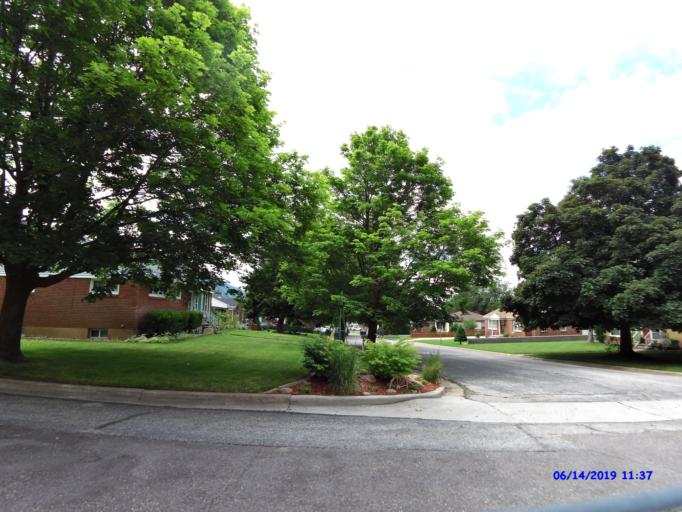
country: US
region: Utah
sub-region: Weber County
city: Ogden
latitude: 41.2522
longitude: -111.9409
